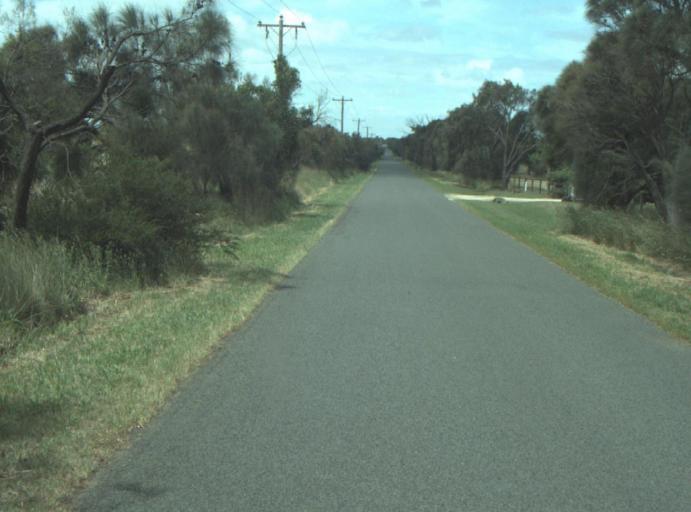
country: AU
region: Victoria
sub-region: Greater Geelong
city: Wandana Heights
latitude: -38.2166
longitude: 144.3133
